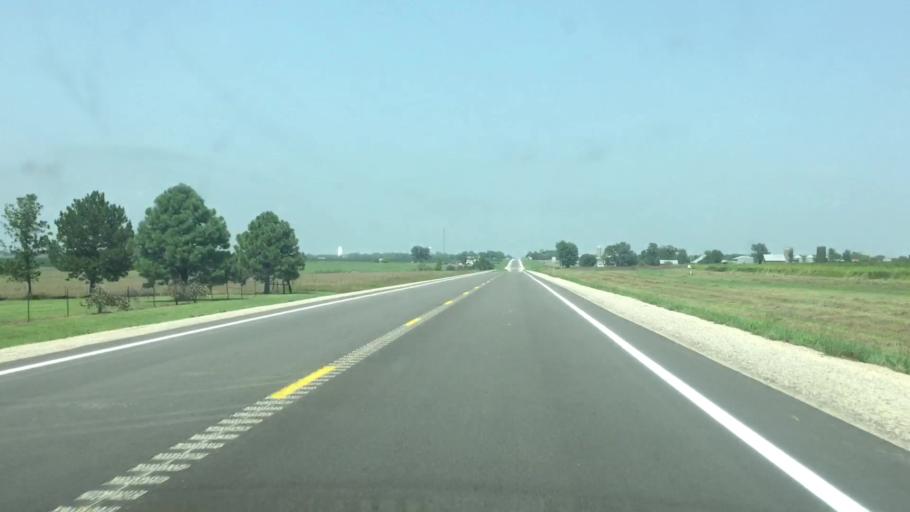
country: US
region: Kansas
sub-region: Anderson County
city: Garnett
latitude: 38.3706
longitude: -95.2487
